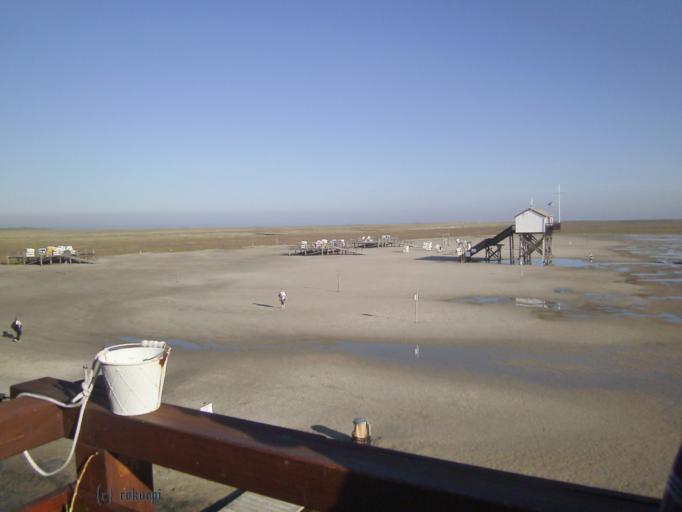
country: DE
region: Schleswig-Holstein
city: Sankt Peter-Ording
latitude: 54.2729
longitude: 8.6561
